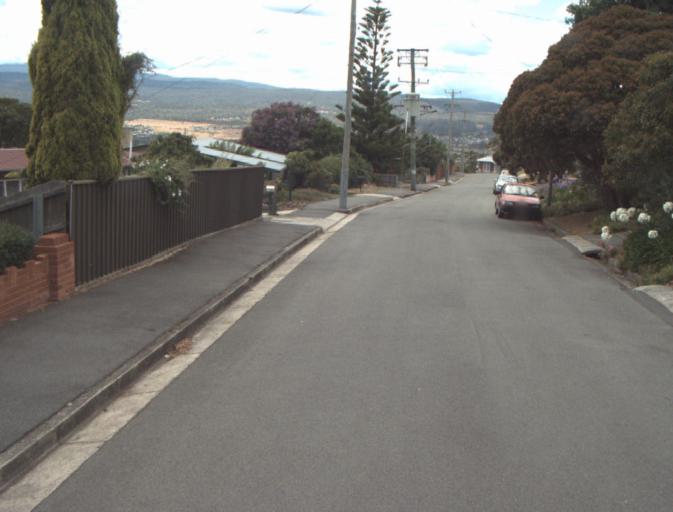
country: AU
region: Tasmania
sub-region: Launceston
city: Launceston
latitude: -41.4398
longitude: 147.1166
